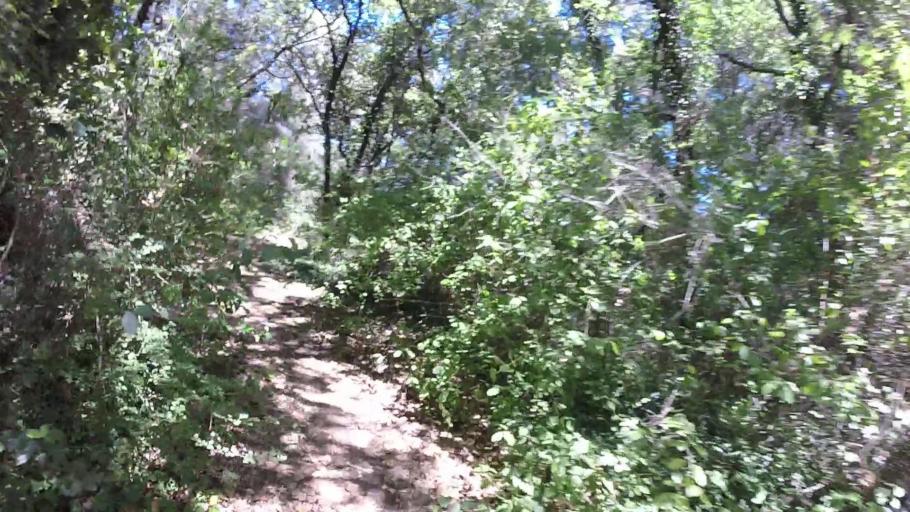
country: FR
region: Provence-Alpes-Cote d'Azur
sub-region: Departement des Alpes-Maritimes
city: Valbonne
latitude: 43.6366
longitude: 7.0197
